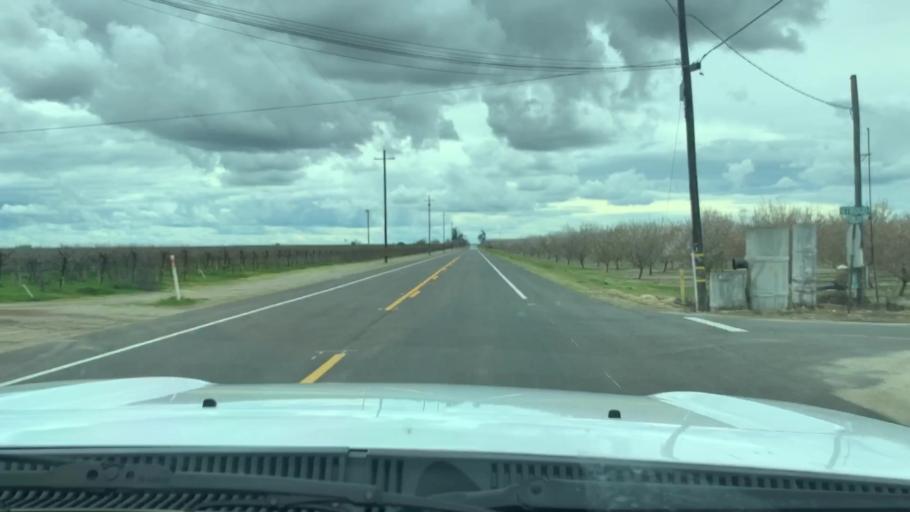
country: US
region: California
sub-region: Fresno County
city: Selma
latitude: 36.5254
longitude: -119.6829
